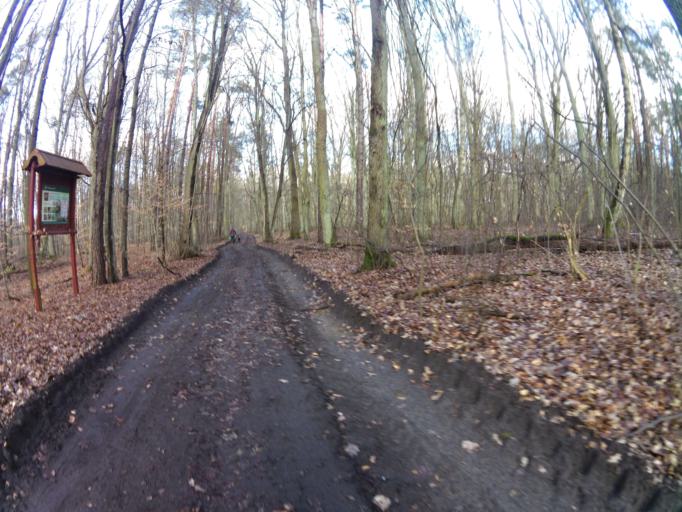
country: PL
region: West Pomeranian Voivodeship
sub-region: Powiat mysliborski
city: Debno
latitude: 52.7511
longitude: 14.7204
